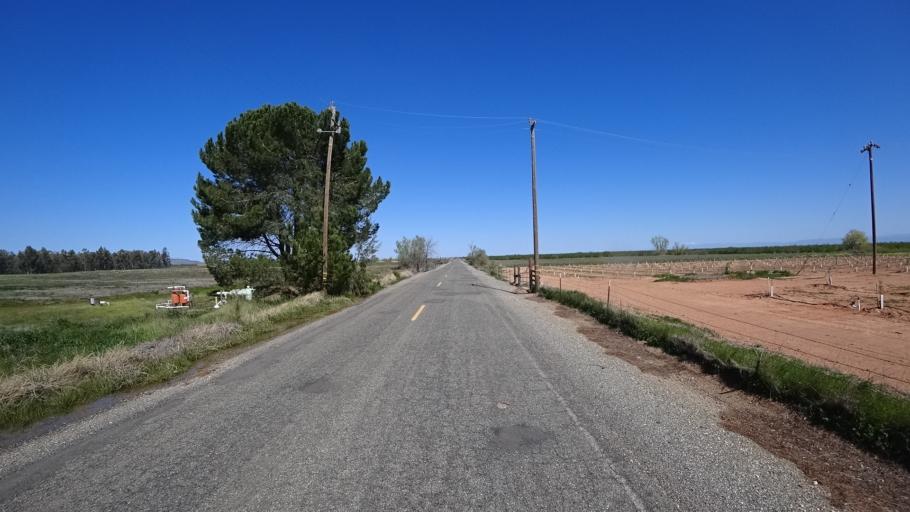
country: US
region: California
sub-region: Glenn County
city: Orland
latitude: 39.6816
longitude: -122.2531
